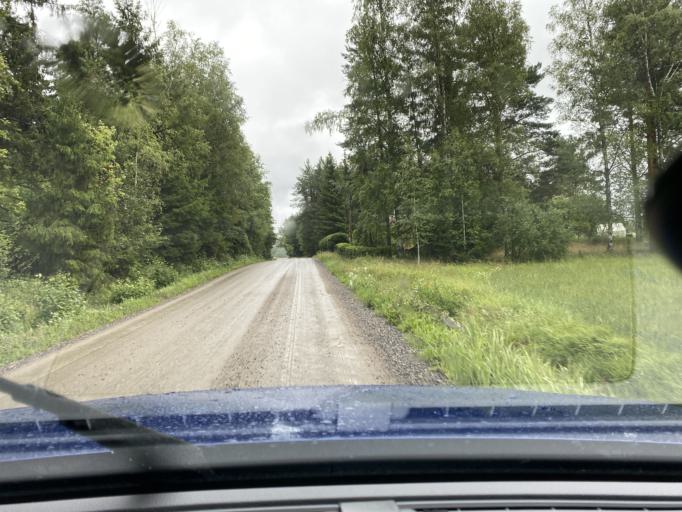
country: FI
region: Pirkanmaa
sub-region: Lounais-Pirkanmaa
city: Punkalaidun
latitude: 61.1482
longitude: 23.2108
